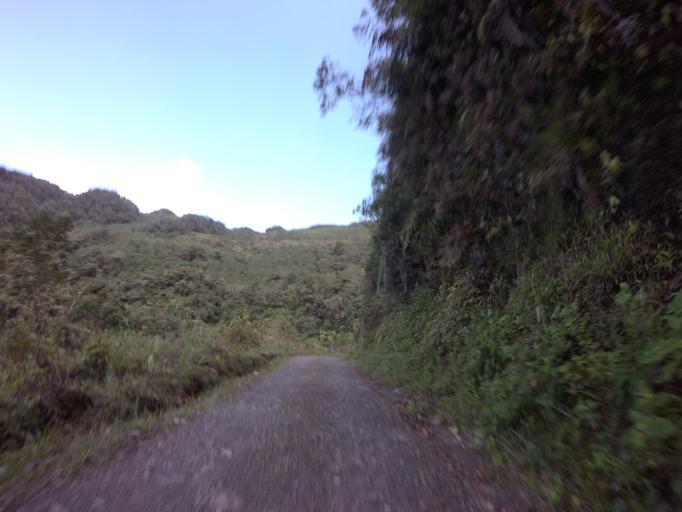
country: CO
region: Caldas
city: Pensilvania
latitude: 5.4508
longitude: -75.1523
